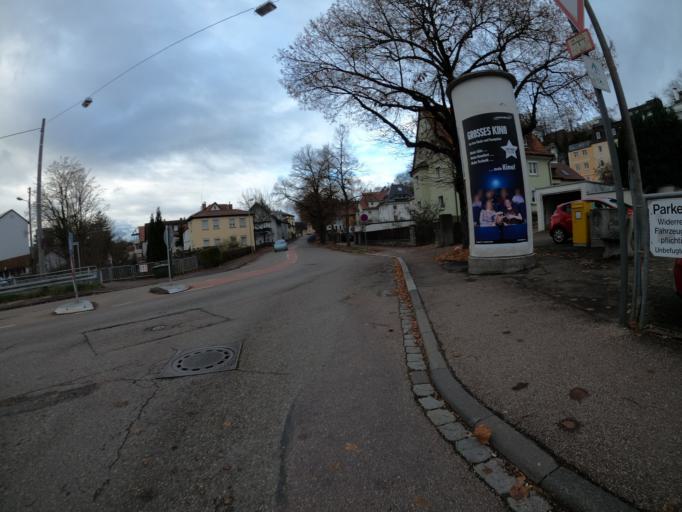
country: DE
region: Baden-Wuerttemberg
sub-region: Regierungsbezirk Stuttgart
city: Schwabisch Gmund
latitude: 48.7955
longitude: 9.8028
